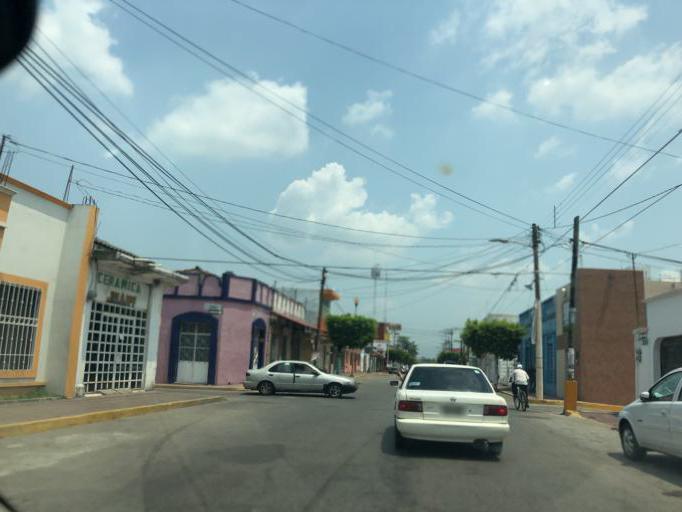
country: MX
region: Tabasco
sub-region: Cardenas
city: Cardenas
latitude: 17.9854
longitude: -93.3769
